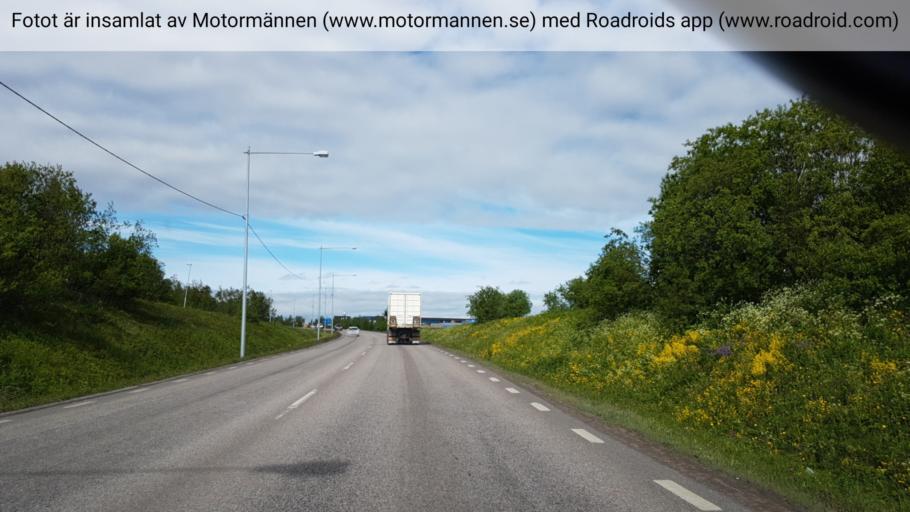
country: SE
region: Norrbotten
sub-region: Kiruna Kommun
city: Kiruna
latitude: 67.8452
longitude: 20.2690
